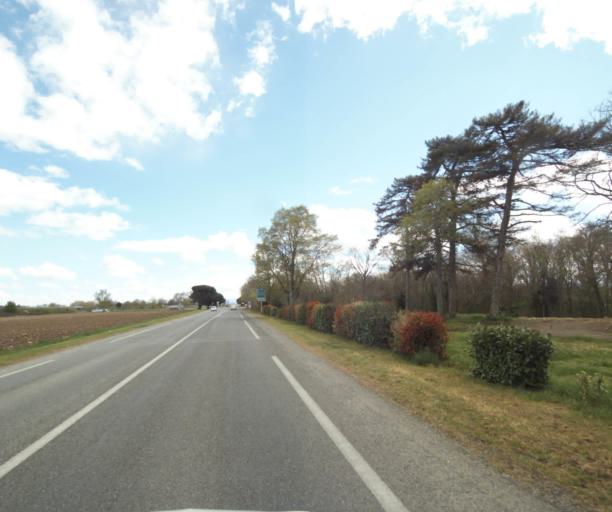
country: FR
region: Midi-Pyrenees
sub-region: Departement de l'Ariege
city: Saverdun
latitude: 43.2293
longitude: 1.6023
